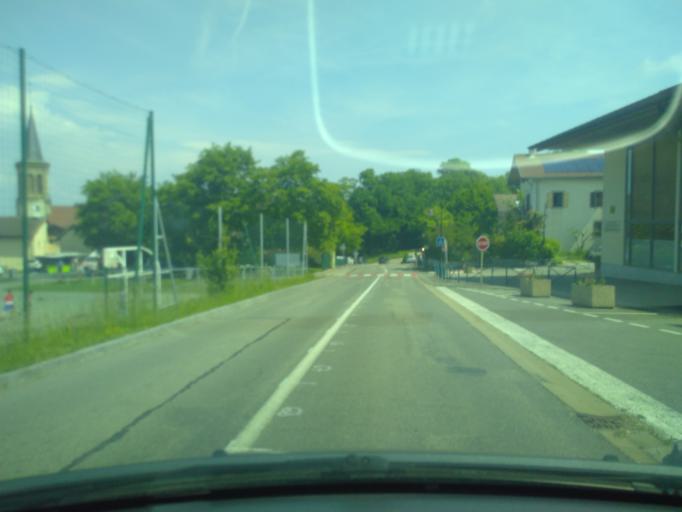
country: FR
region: Rhone-Alpes
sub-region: Departement de la Haute-Savoie
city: Archamps
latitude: 46.1341
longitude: 6.1329
